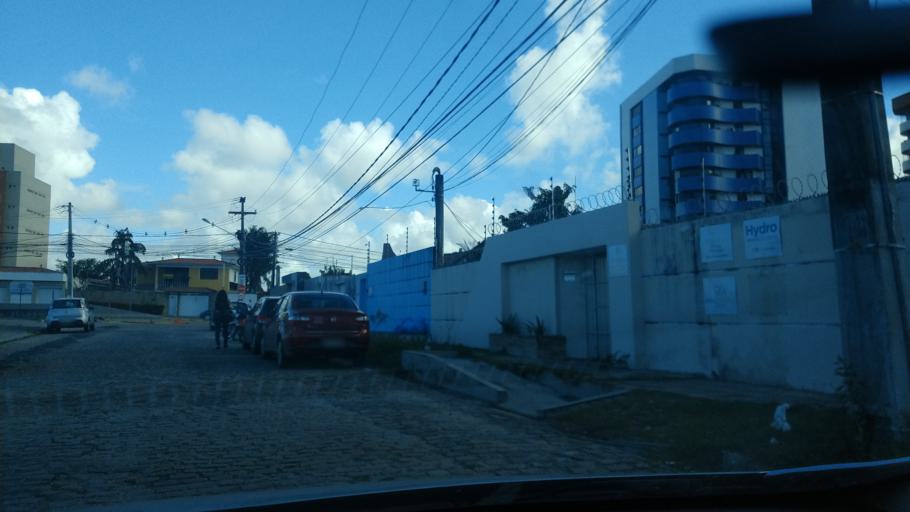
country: BR
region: Rio Grande do Norte
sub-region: Natal
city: Natal
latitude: -5.8308
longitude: -35.2183
